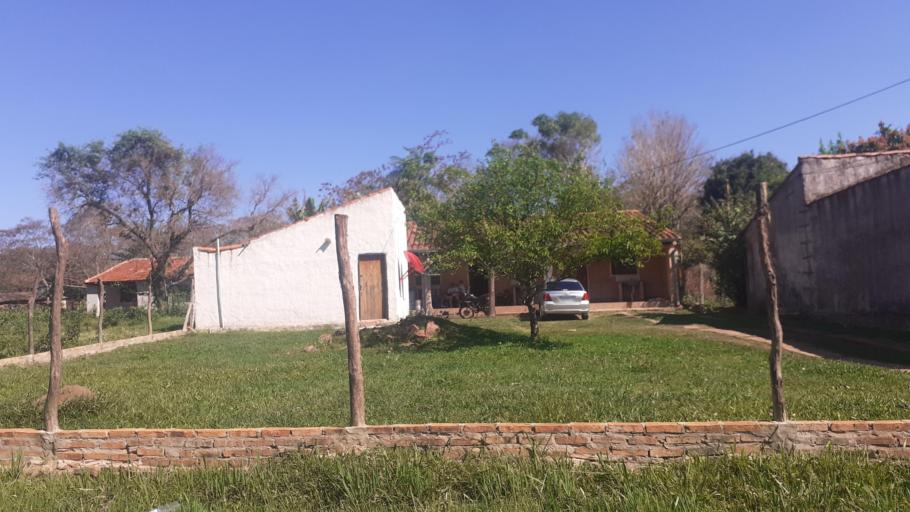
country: PY
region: Misiones
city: San Juan Bautista
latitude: -26.6704
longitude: -57.1247
